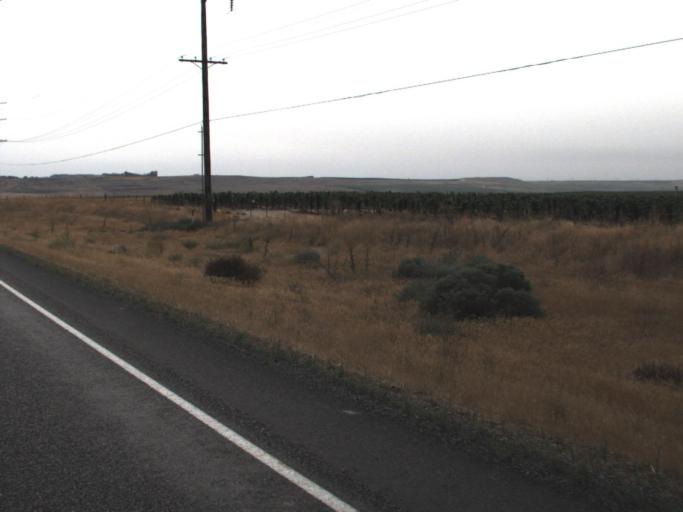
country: US
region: Oregon
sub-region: Morrow County
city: Irrigon
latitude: 45.9880
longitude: -119.6029
